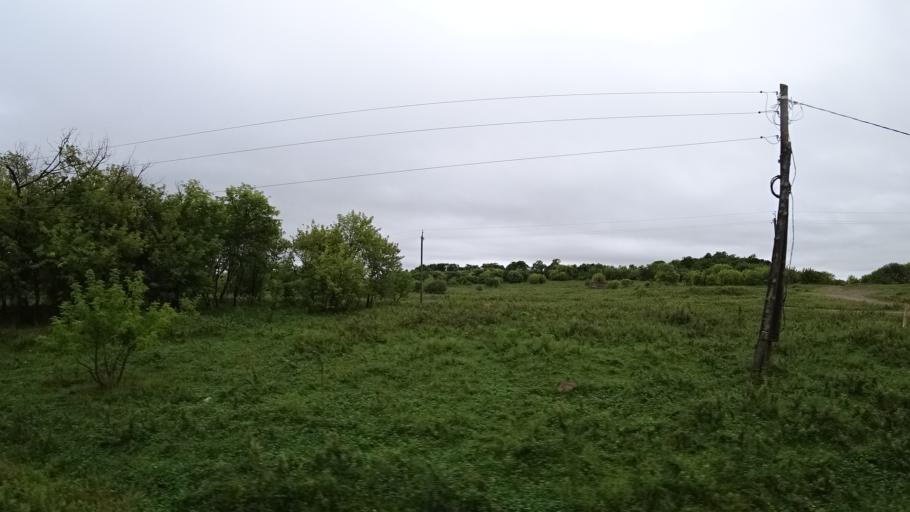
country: RU
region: Primorskiy
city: Monastyrishche
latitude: 44.2570
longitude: 132.4196
